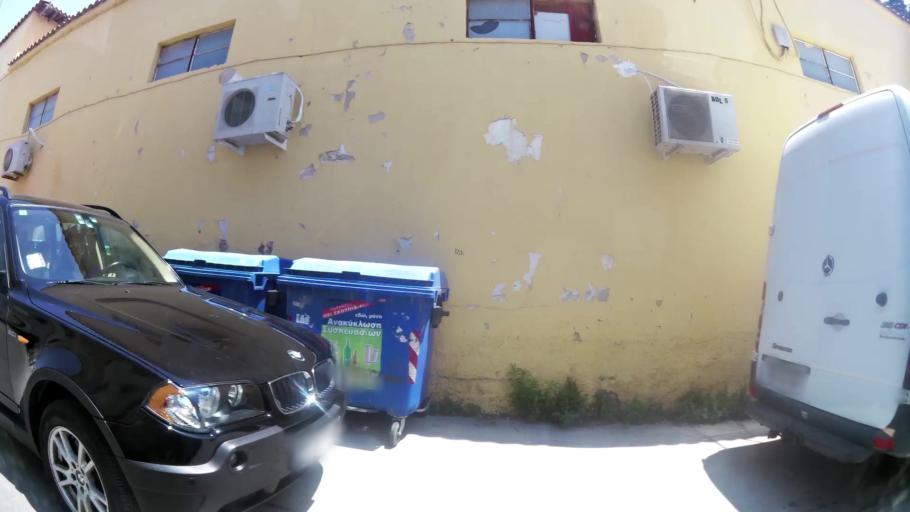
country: GR
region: Central Macedonia
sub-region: Nomos Thessalonikis
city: Epanomi
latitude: 40.4284
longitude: 22.9266
